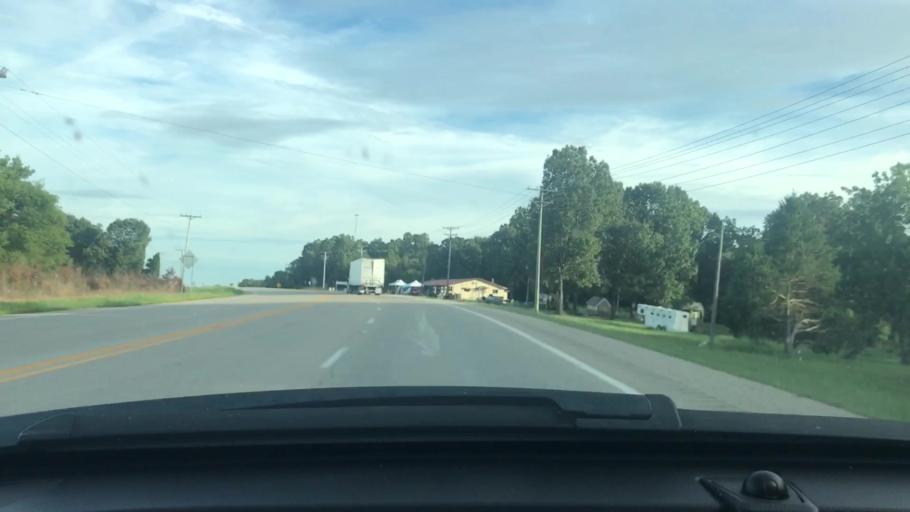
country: US
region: Arkansas
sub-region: Lawrence County
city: Hoxie
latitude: 36.1292
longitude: -91.1579
